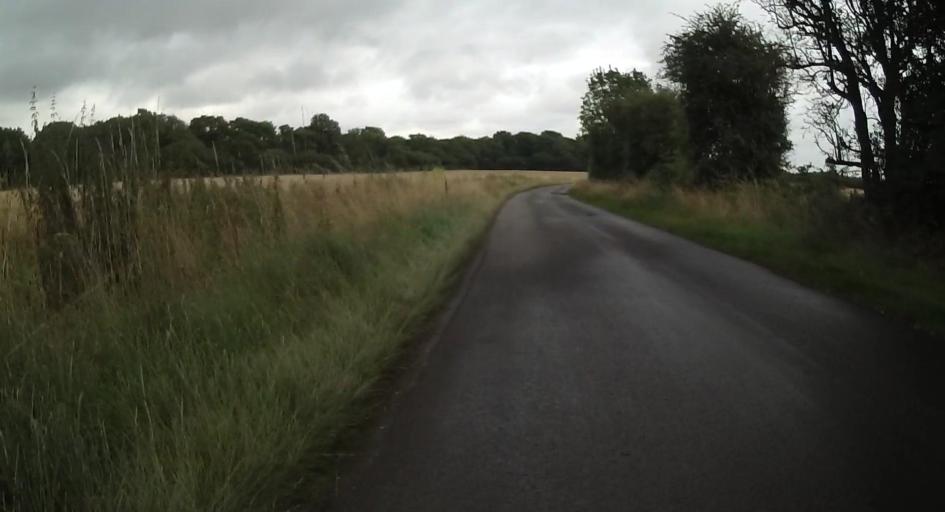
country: GB
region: England
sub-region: Hampshire
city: Andover
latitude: 51.2014
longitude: -1.4151
